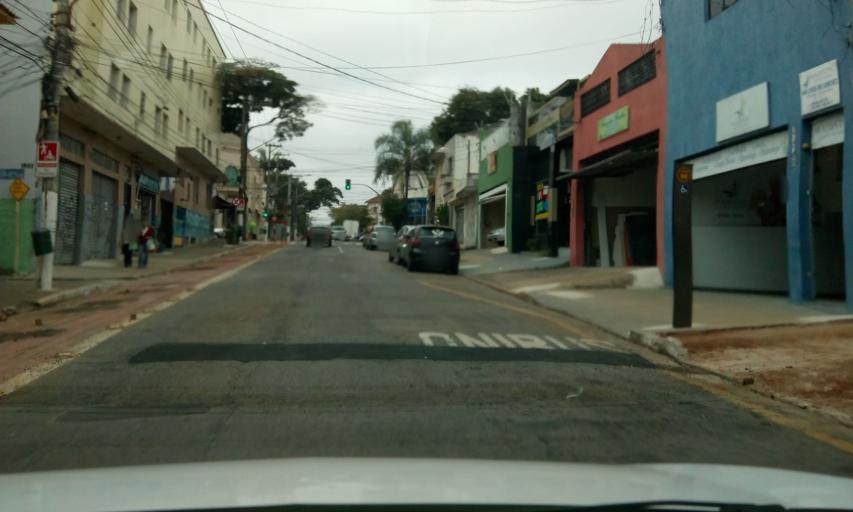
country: BR
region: Sao Paulo
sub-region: Sao Paulo
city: Sao Paulo
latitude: -23.5510
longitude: -46.5873
